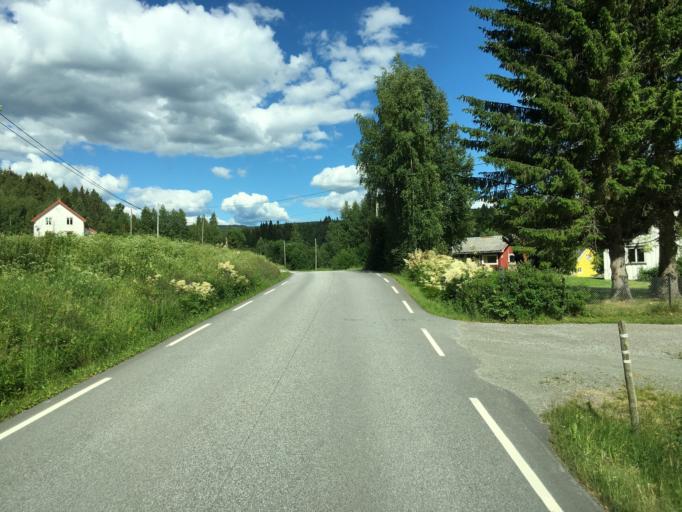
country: NO
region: Oppland
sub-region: Sondre Land
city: Hov
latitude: 60.6180
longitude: 10.3371
